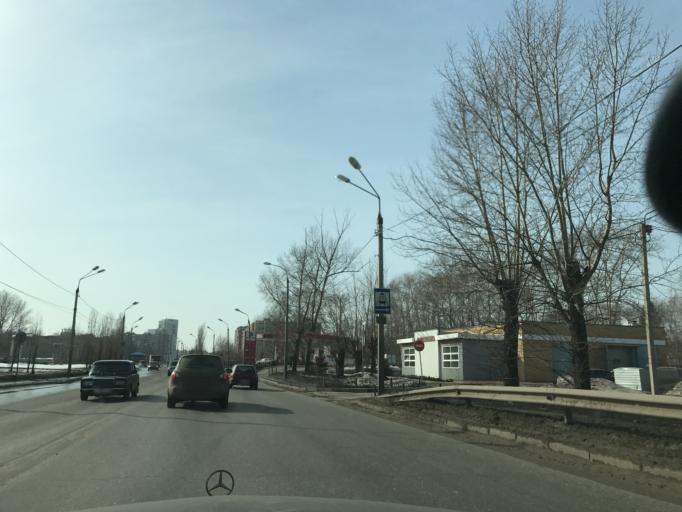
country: RU
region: Nizjnij Novgorod
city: Gorbatovka
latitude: 56.2636
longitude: 43.8686
